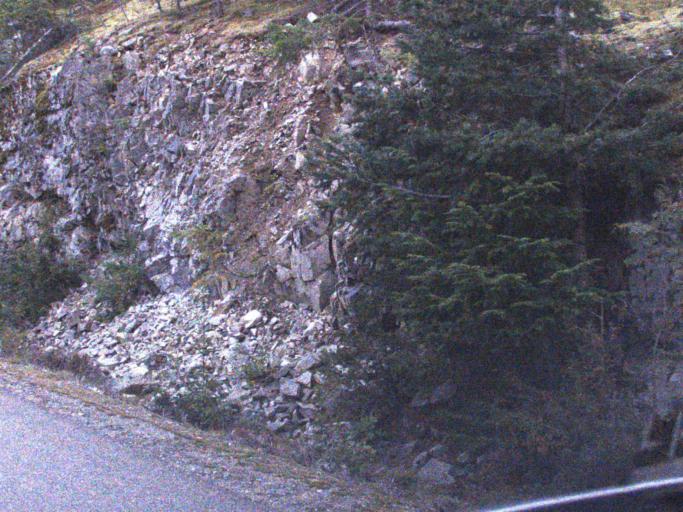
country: US
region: Washington
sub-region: Snohomish County
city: Darrington
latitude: 48.6676
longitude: -120.8736
